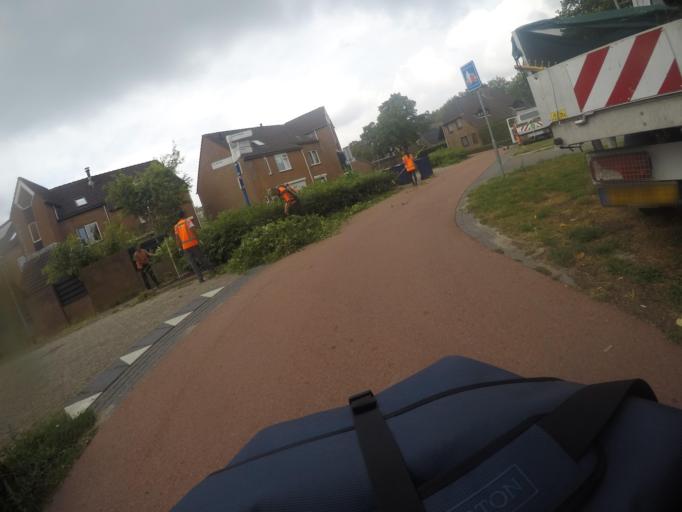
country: NL
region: Flevoland
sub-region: Gemeente Almere
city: Almere Stad
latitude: 52.3478
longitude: 5.2175
